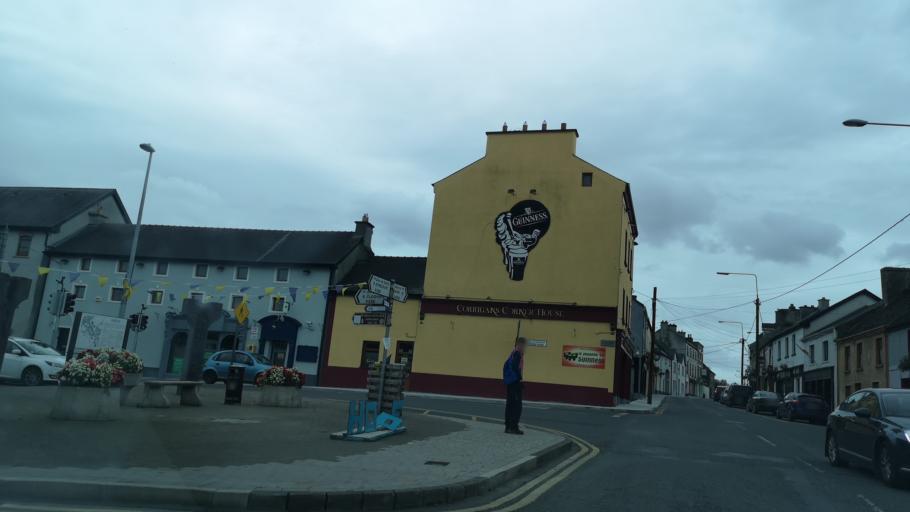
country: IE
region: Leinster
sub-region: Uibh Fhaili
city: Banagher
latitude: 53.1899
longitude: -7.9871
